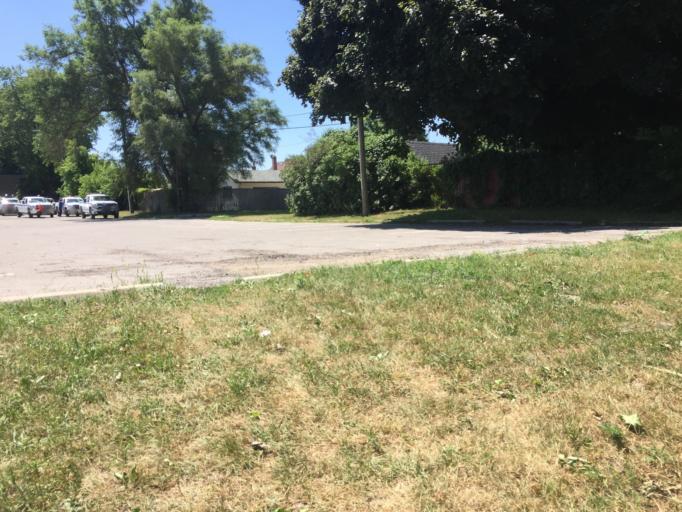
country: CA
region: Ontario
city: Oshawa
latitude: 43.8984
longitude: -78.8719
